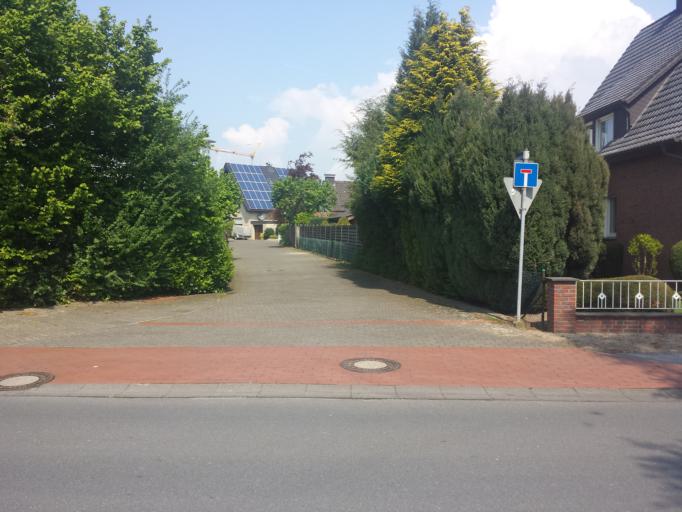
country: DE
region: North Rhine-Westphalia
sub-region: Regierungsbezirk Detmold
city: Guetersloh
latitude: 51.9040
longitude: 8.4239
